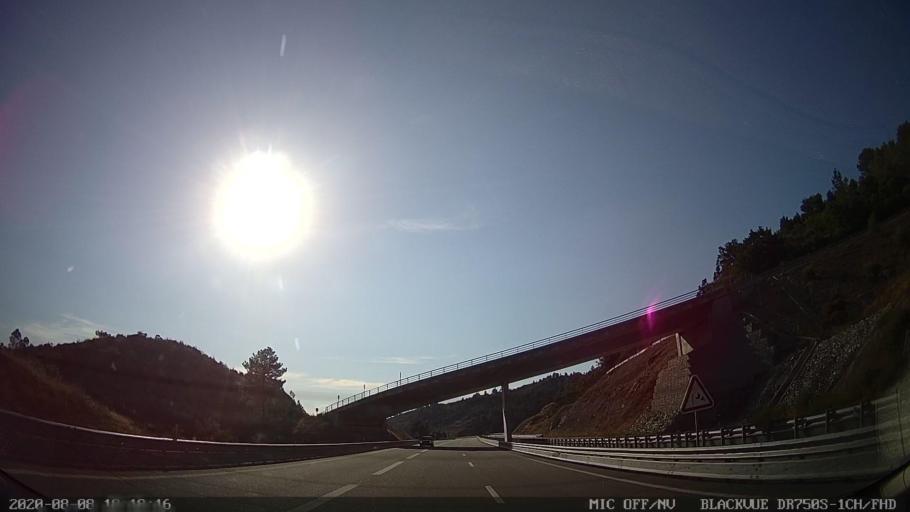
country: PT
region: Porto
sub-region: Baiao
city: Valadares
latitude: 41.2514
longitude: -7.9712
